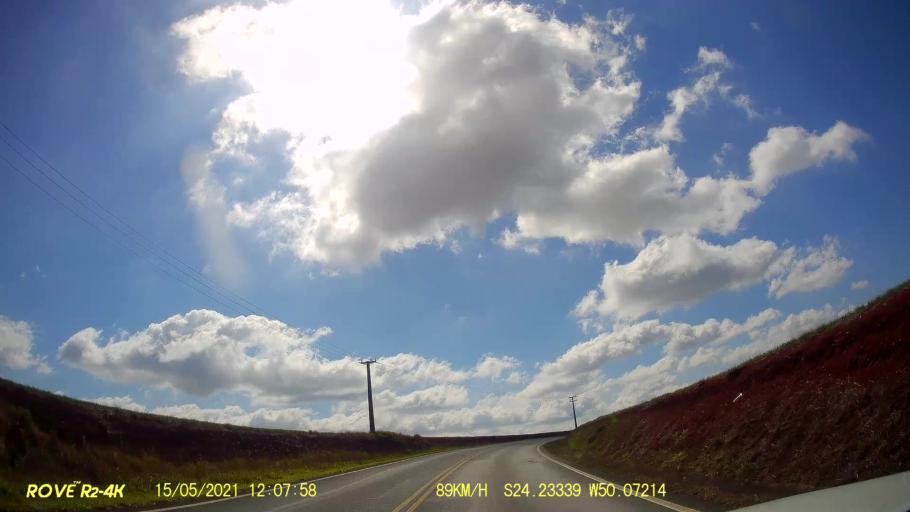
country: BR
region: Parana
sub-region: Pirai Do Sul
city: Pirai do Sul
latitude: -24.2333
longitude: -50.0721
